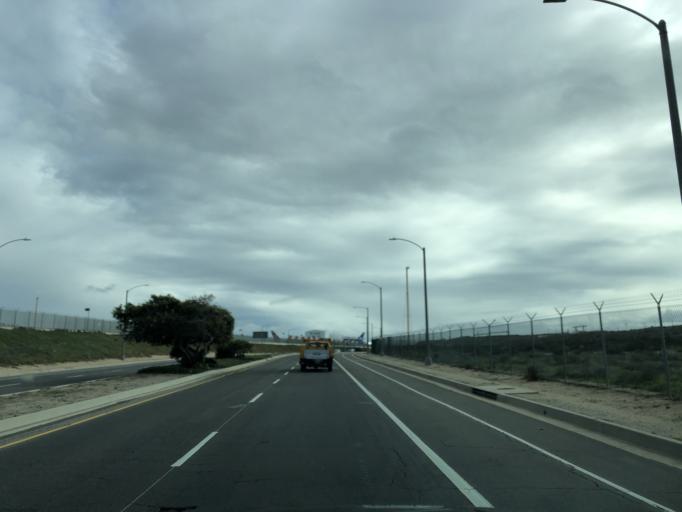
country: US
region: California
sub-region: Los Angeles County
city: Marina del Rey
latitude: 33.9492
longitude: -118.4377
